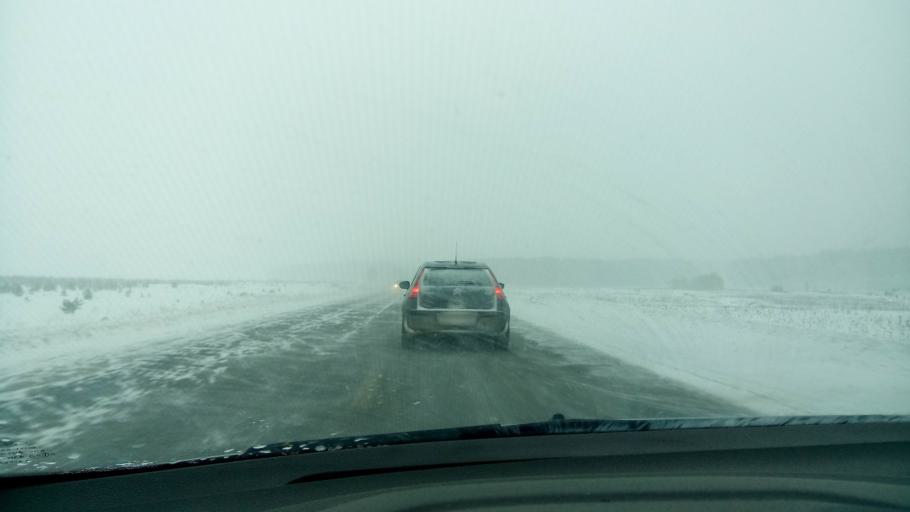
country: RU
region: Sverdlovsk
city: Beloyarskiy
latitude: 56.7713
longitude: 61.4778
